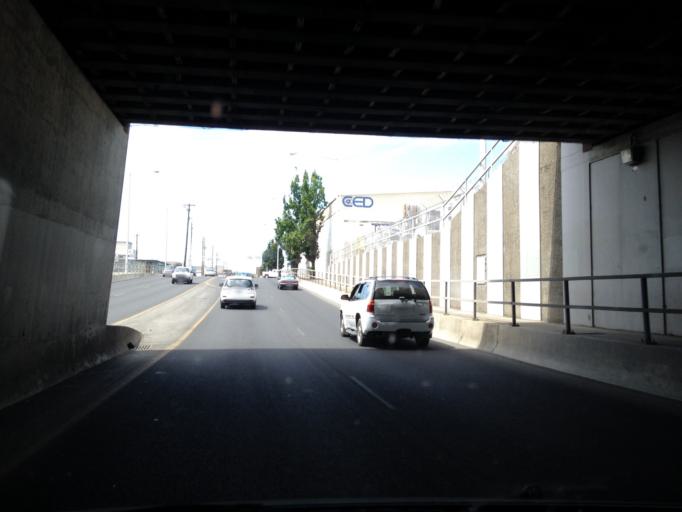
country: US
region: Washington
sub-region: Yakima County
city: Yakima
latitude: 46.5994
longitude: -120.5066
